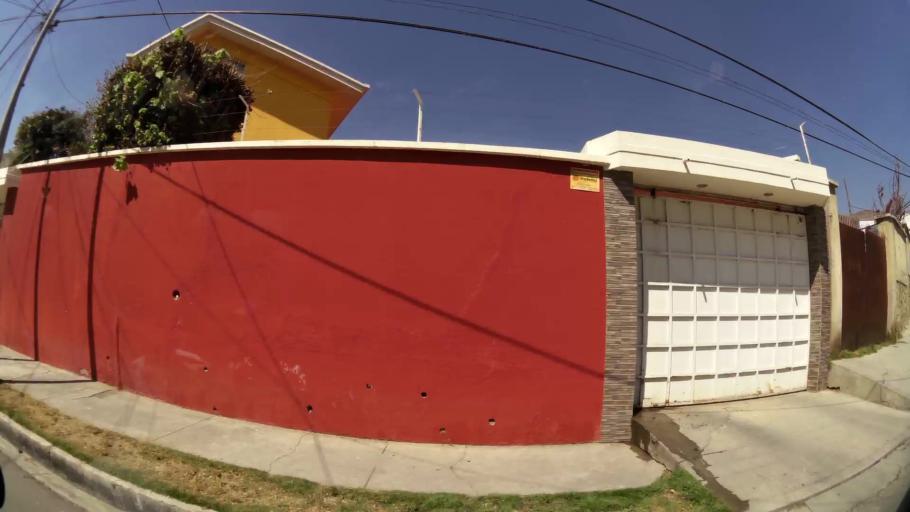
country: BO
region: La Paz
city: La Paz
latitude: -16.5421
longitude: -68.0588
